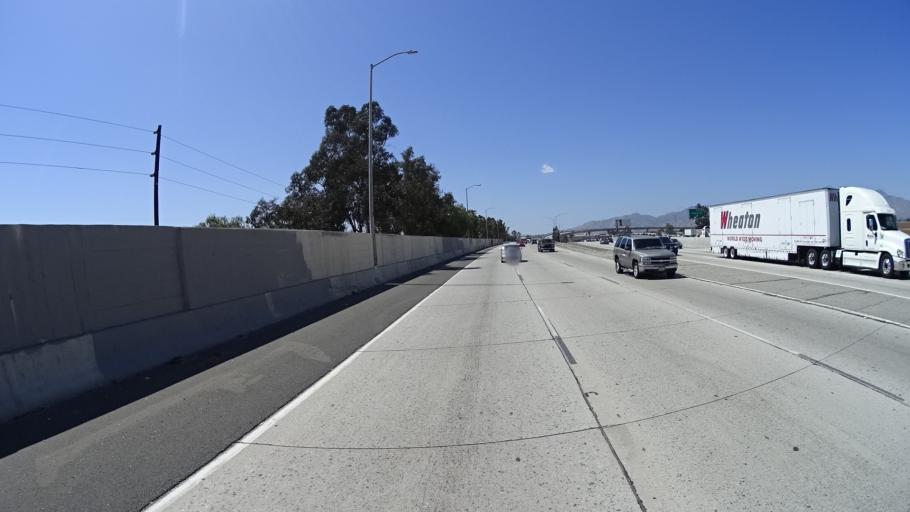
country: US
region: California
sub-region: Los Angeles County
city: San Fernando
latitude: 34.2609
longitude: -118.4399
